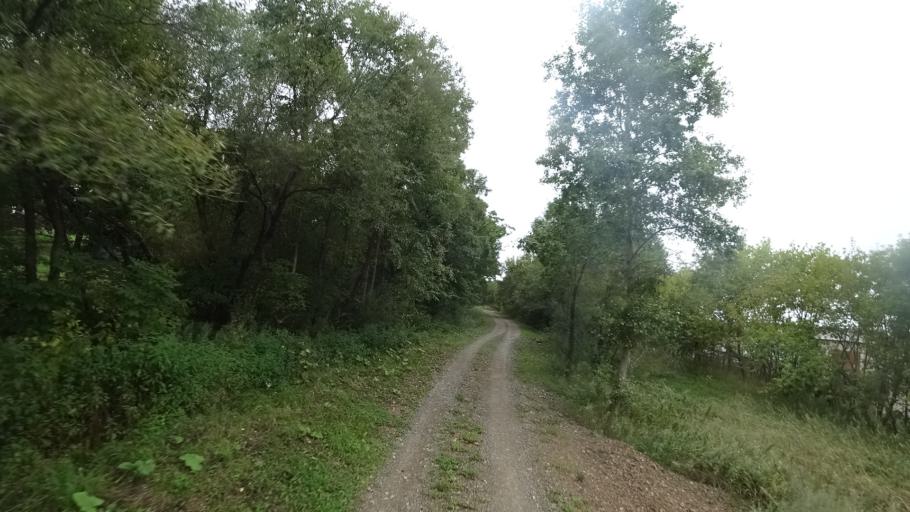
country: RU
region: Primorskiy
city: Monastyrishche
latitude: 44.2681
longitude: 132.4563
